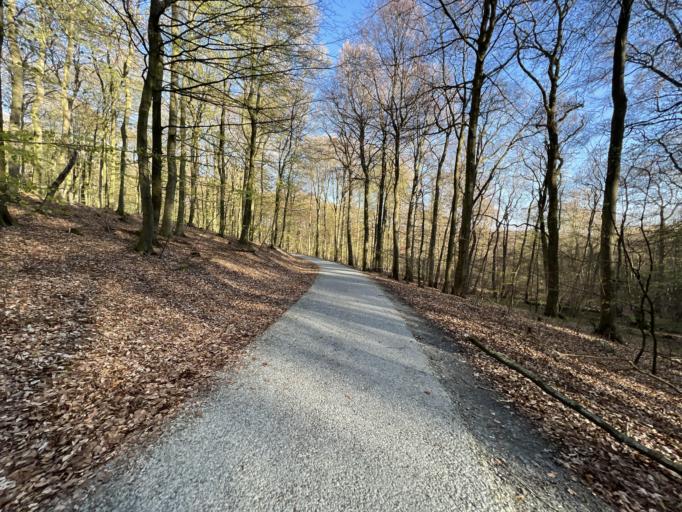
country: DE
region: Mecklenburg-Vorpommern
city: Sassnitz
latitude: 54.5307
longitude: 13.6375
